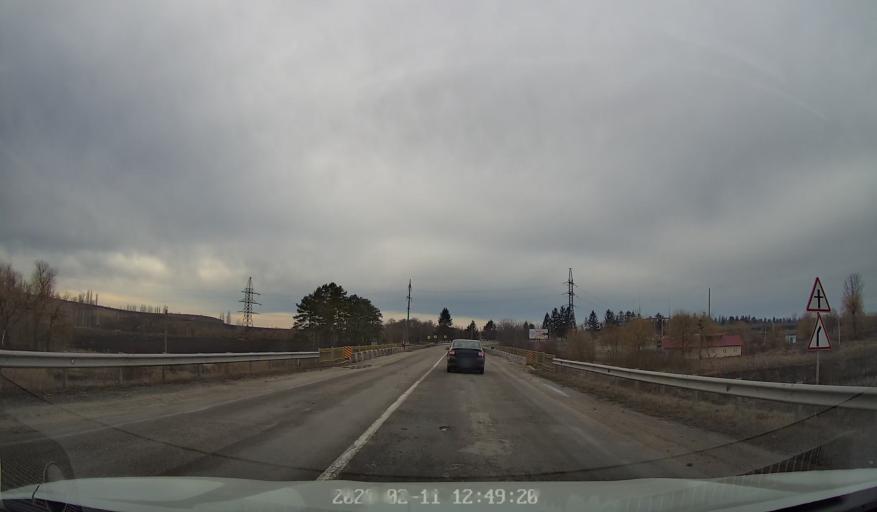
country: MD
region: Briceni
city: Briceni
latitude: 48.2849
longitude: 27.1352
